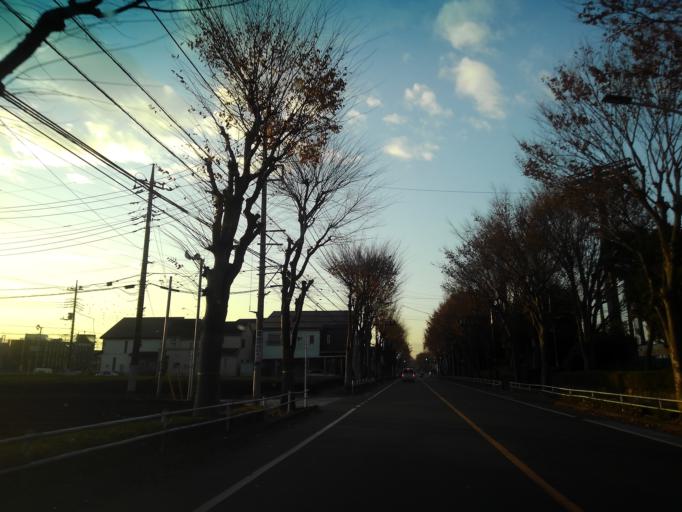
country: JP
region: Tokyo
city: Higashimurayama-shi
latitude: 35.7416
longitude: 139.4447
